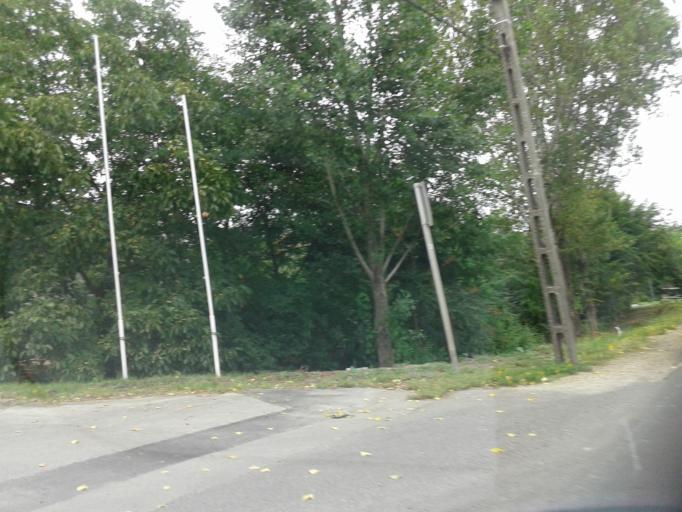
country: HU
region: Bacs-Kiskun
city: Solt
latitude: 46.8021
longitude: 19.0135
